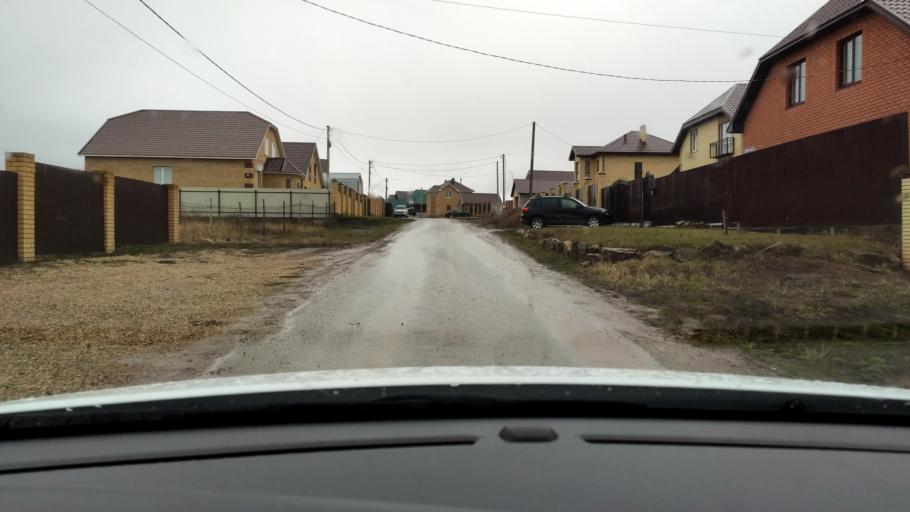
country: RU
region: Tatarstan
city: Vysokaya Gora
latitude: 55.9020
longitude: 49.3178
